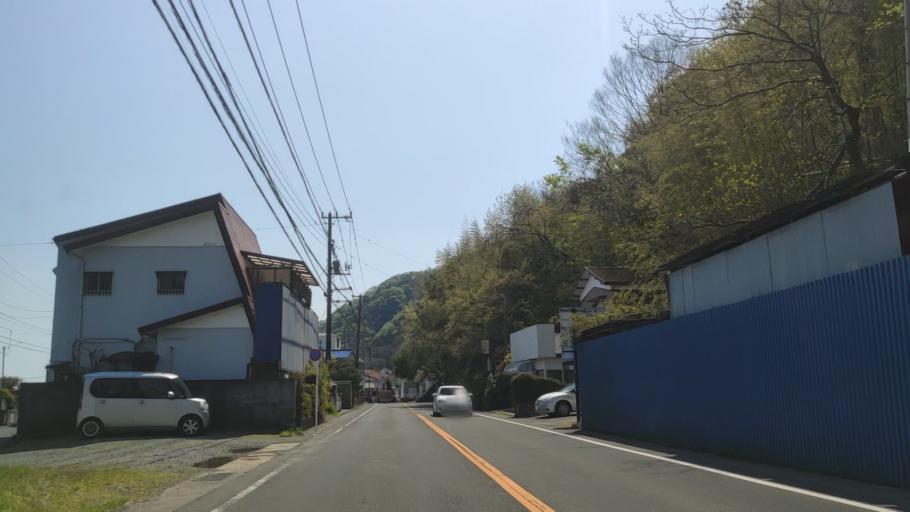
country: JP
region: Kanagawa
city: Hiratsuka
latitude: 35.3277
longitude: 139.3161
